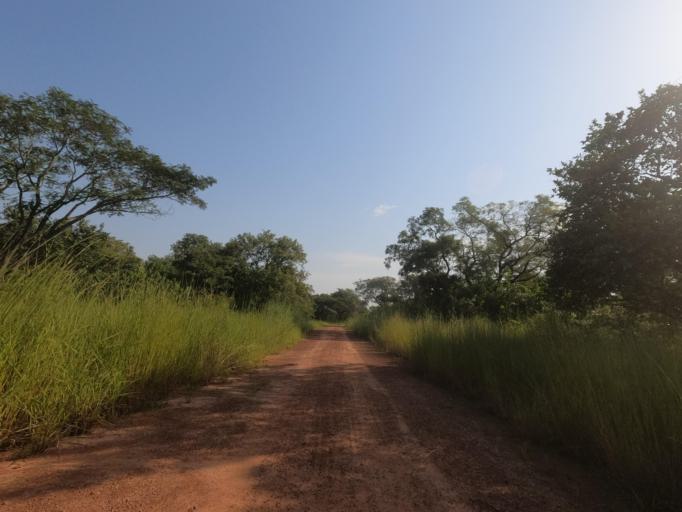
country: SN
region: Sedhiou
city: Sedhiou
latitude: 12.4337
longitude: -15.7376
